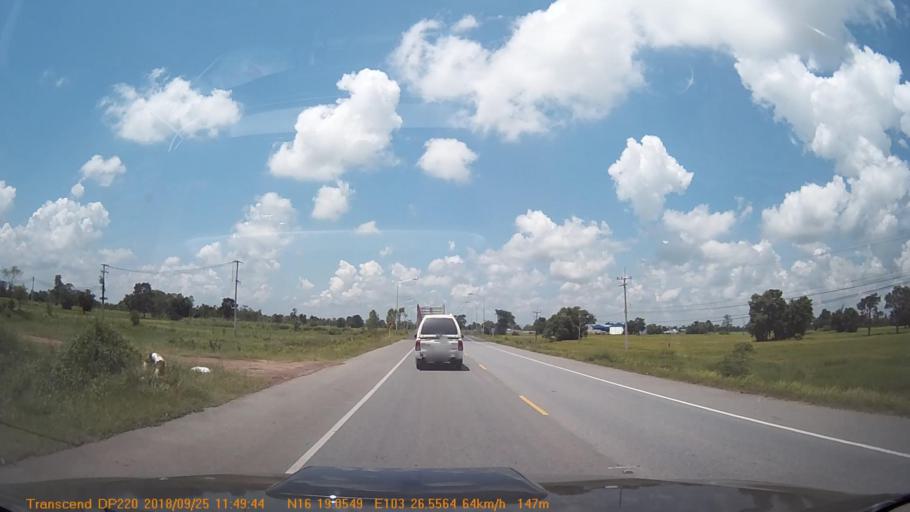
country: TH
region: Kalasin
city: Khong Chai
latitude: 16.3176
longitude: 103.4426
